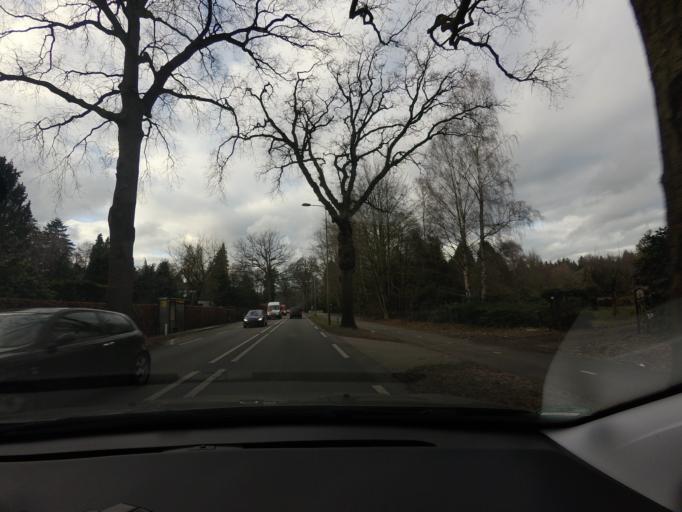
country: NL
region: Gelderland
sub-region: Gemeente Lochem
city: Eefde
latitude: 52.1817
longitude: 6.2152
